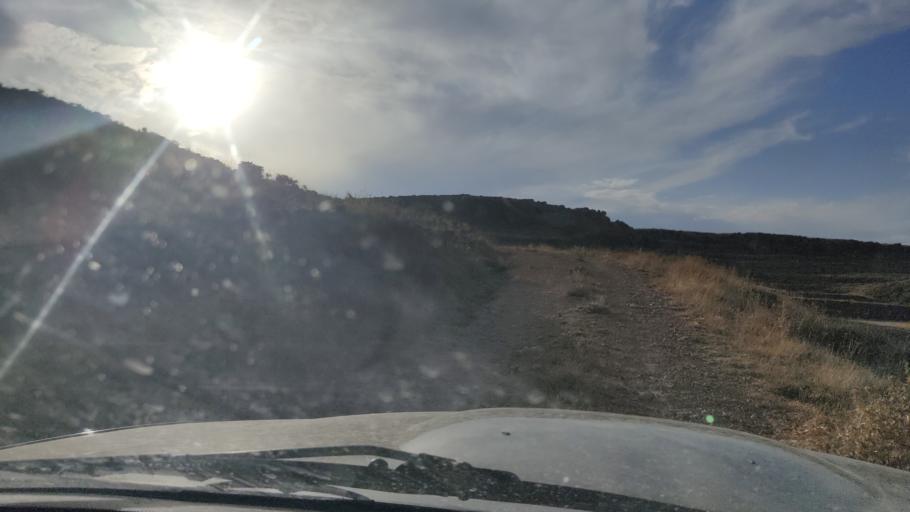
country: ES
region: Aragon
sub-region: Provincia de Teruel
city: Monforte de Moyuela
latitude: 41.0556
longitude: -0.9734
